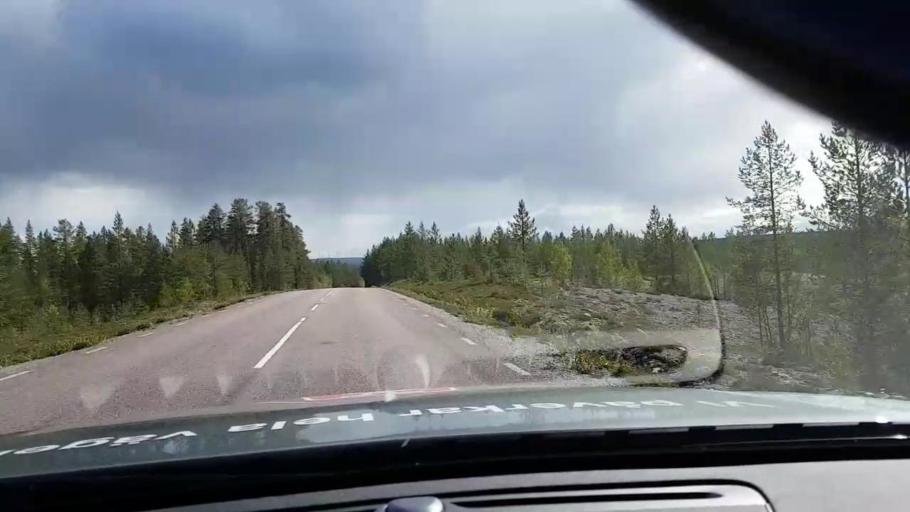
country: SE
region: Vaesterbotten
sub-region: Asele Kommun
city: Asele
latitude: 63.8854
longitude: 17.3524
